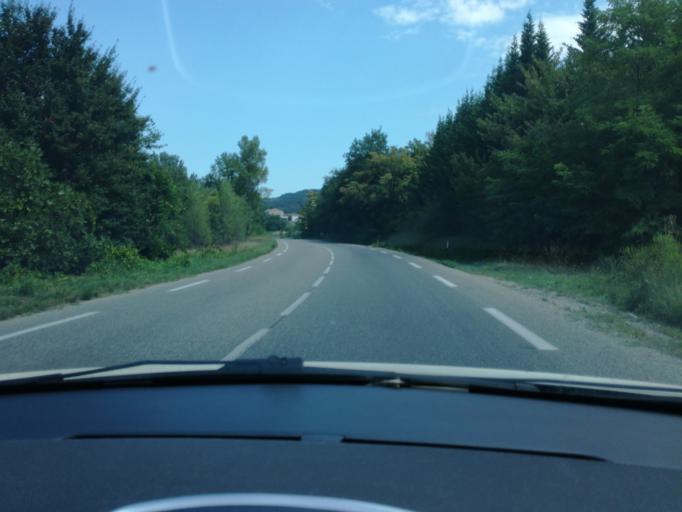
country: FR
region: Rhone-Alpes
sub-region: Departement de l'Ardeche
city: Ruoms
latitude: 44.4782
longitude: 4.3767
